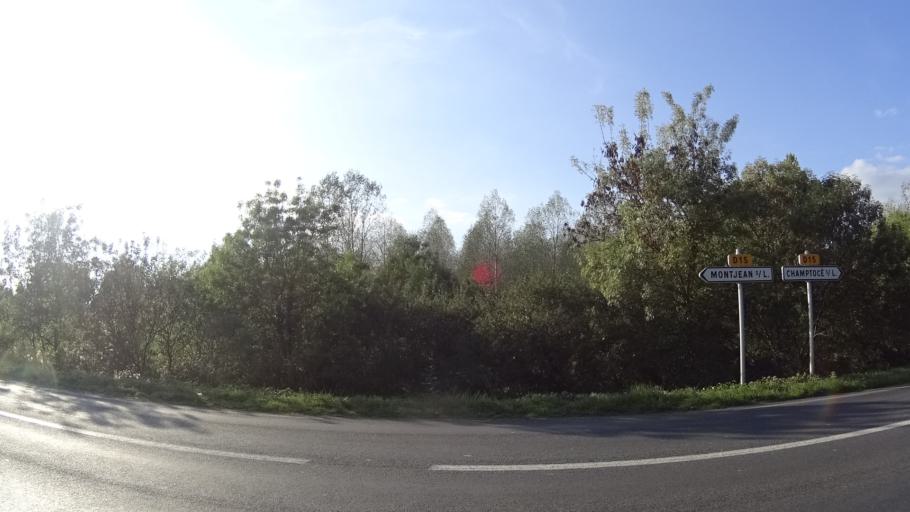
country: FR
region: Pays de la Loire
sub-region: Departement de Maine-et-Loire
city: Montjean-sur-Loire
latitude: 47.3969
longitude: -0.8577
